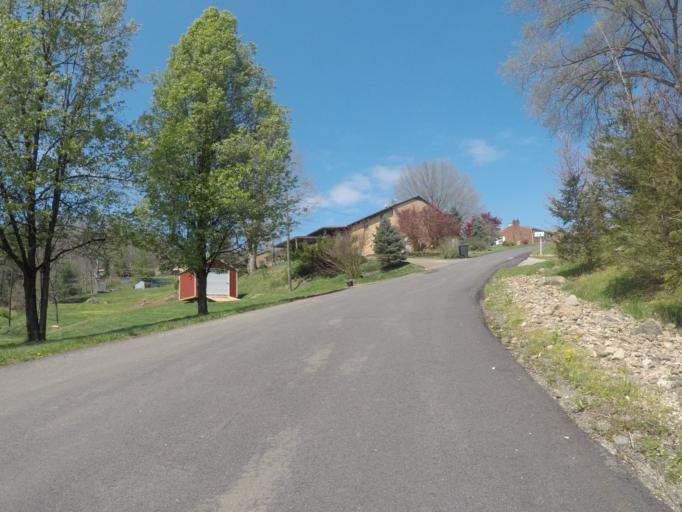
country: US
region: Ohio
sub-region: Lawrence County
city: Burlington
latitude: 38.3800
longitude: -82.5282
